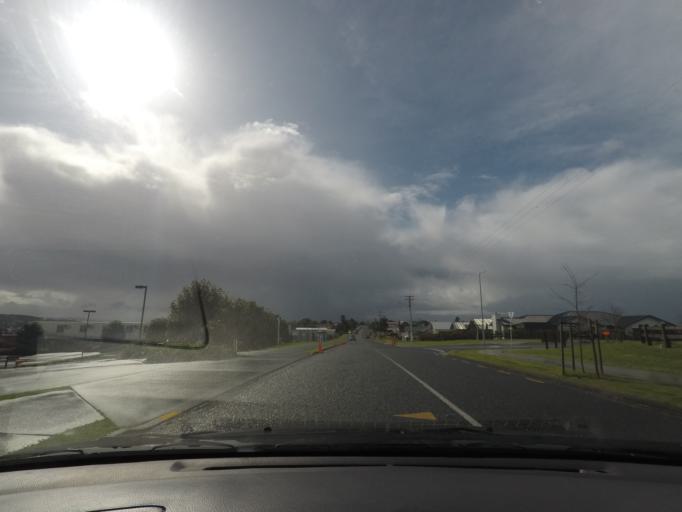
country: NZ
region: Auckland
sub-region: Auckland
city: Warkworth
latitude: -36.4290
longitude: 174.7244
